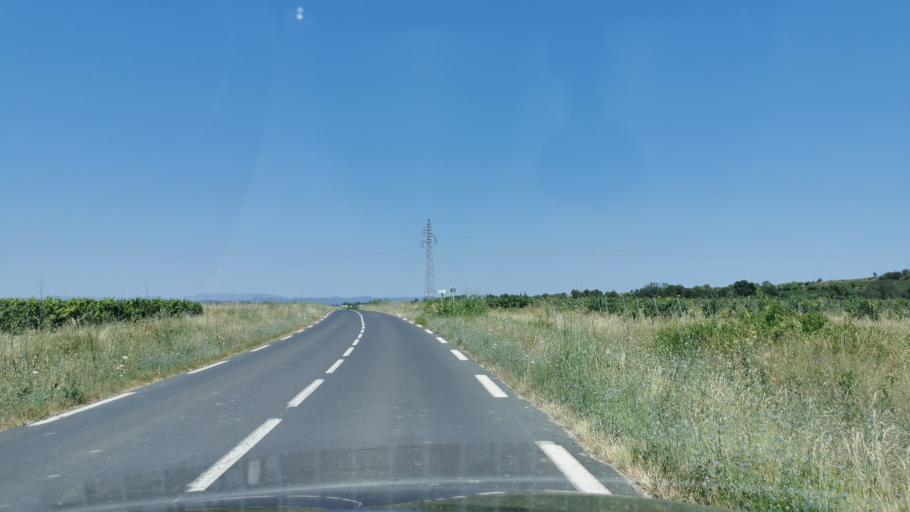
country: FR
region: Languedoc-Roussillon
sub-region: Departement de l'Herault
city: Maureilhan
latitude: 43.3706
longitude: 3.1138
